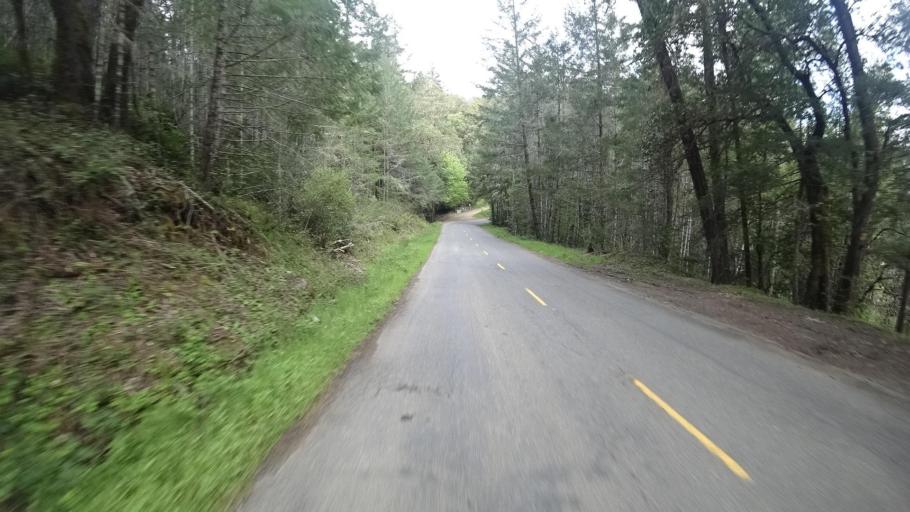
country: US
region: California
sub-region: Humboldt County
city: Redway
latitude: 40.1390
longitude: -123.6302
